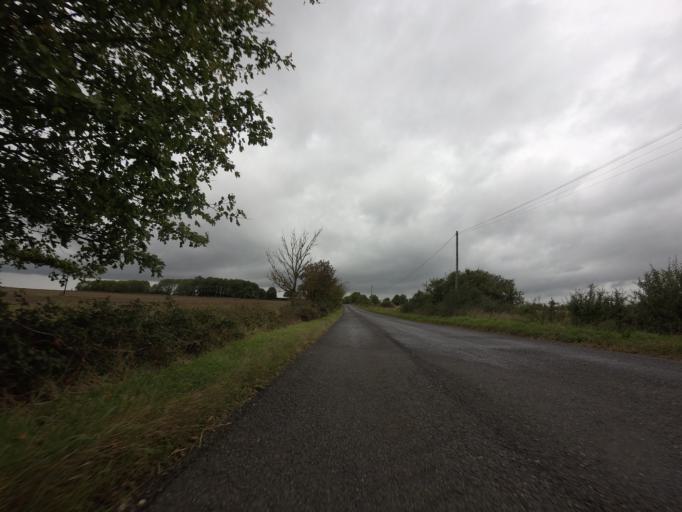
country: GB
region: England
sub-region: Cambridgeshire
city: Wimpole
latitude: 52.1747
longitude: -0.0268
